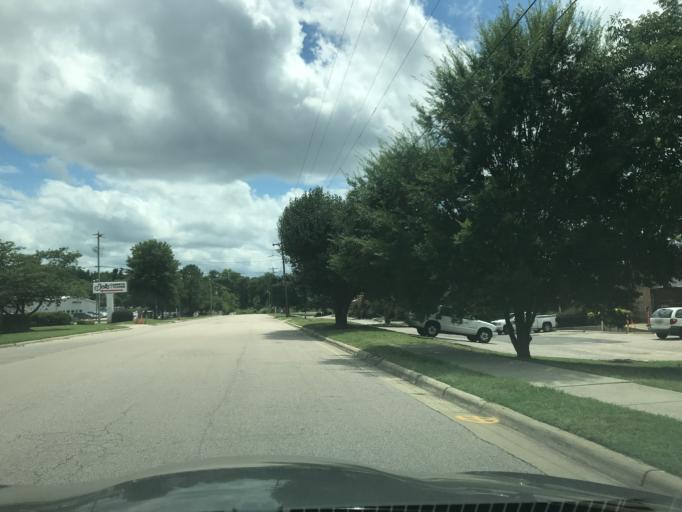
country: US
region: North Carolina
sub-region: Wake County
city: Raleigh
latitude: 35.8171
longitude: -78.6206
